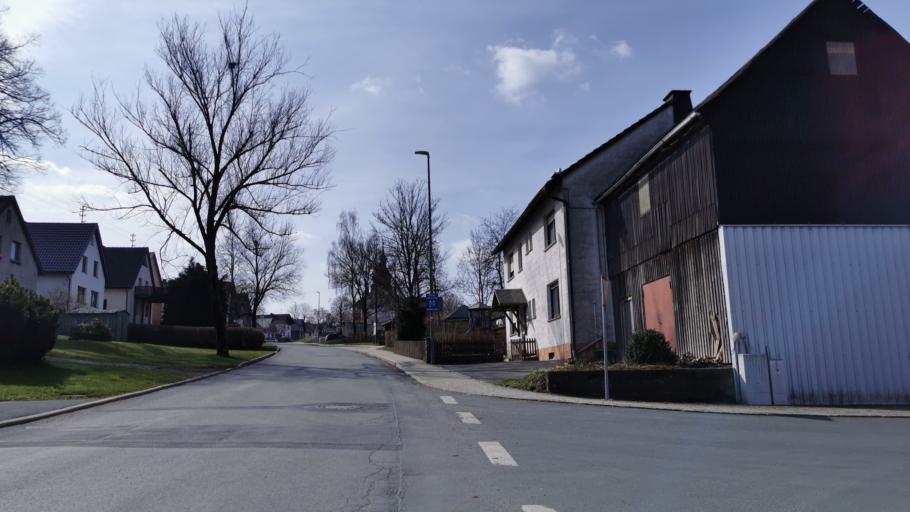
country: DE
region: Bavaria
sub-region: Upper Franconia
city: Teuschnitz
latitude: 50.4140
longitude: 11.3363
